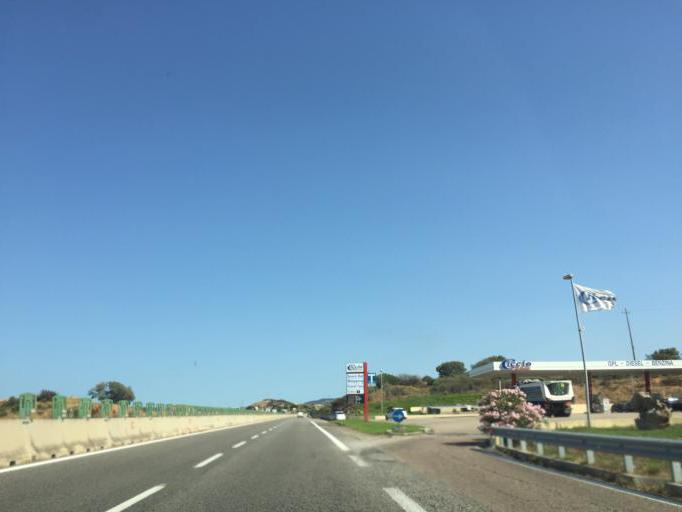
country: IT
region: Sardinia
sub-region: Provincia di Olbia-Tempio
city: Olbia
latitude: 40.8877
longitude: 9.4927
